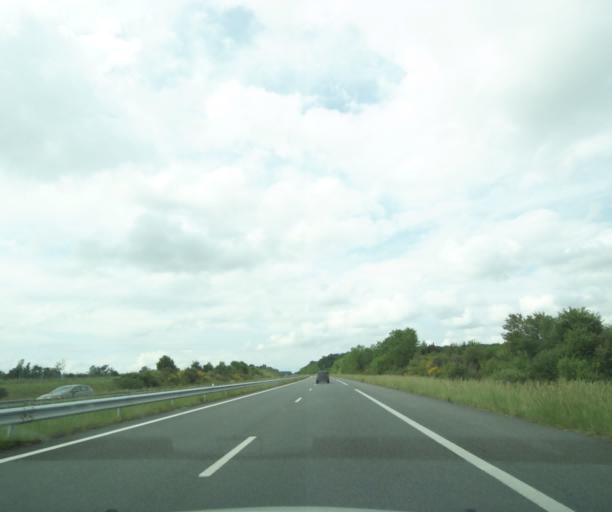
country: FR
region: Centre
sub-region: Departement du Cher
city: Orval
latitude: 46.7938
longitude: 2.4138
